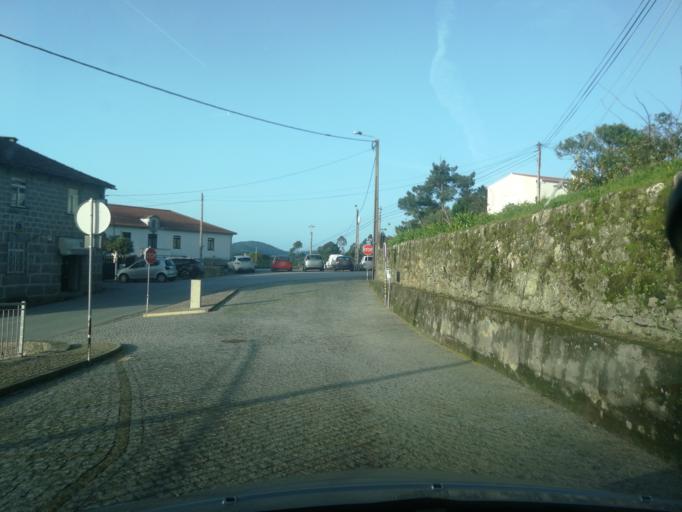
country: PT
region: Braga
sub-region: Barcelos
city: Galegos
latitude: 41.5164
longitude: -8.5586
